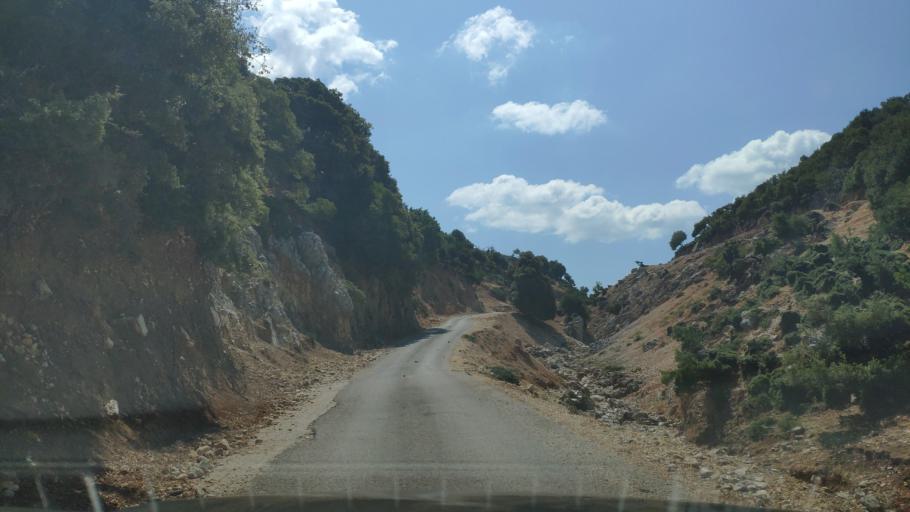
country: GR
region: West Greece
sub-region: Nomos Aitolias kai Akarnanias
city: Monastirakion
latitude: 38.8118
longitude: 20.9392
